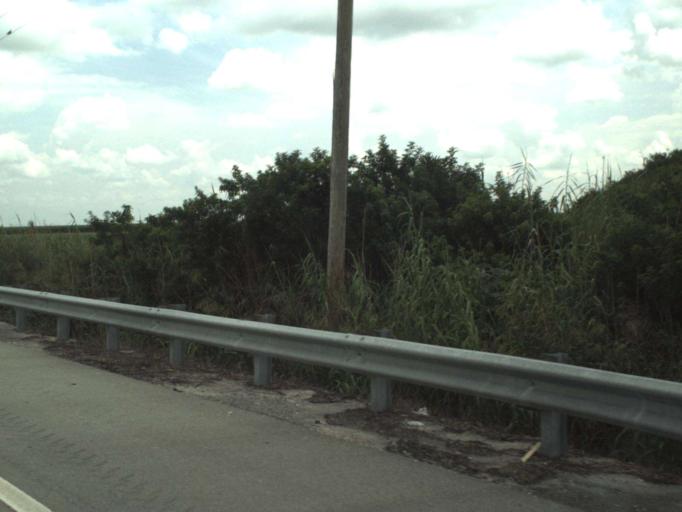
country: US
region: Florida
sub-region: Palm Beach County
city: Pahokee
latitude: 26.7570
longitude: -80.4897
